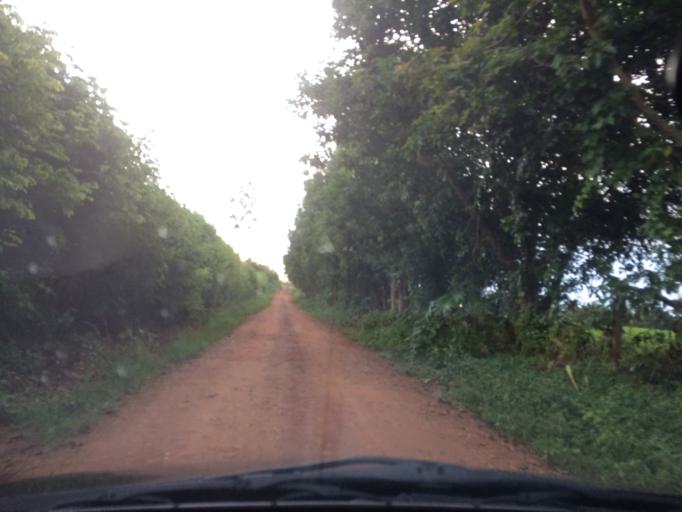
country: BR
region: Sao Paulo
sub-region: Casa Branca
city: Casa Branca
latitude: -21.7580
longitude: -47.1200
